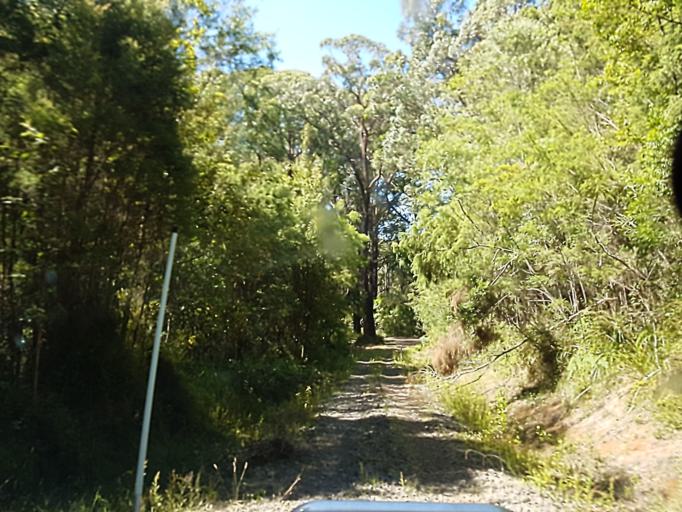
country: AU
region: Victoria
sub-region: Colac-Otway
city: Apollo Bay
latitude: -38.6735
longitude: 143.3536
